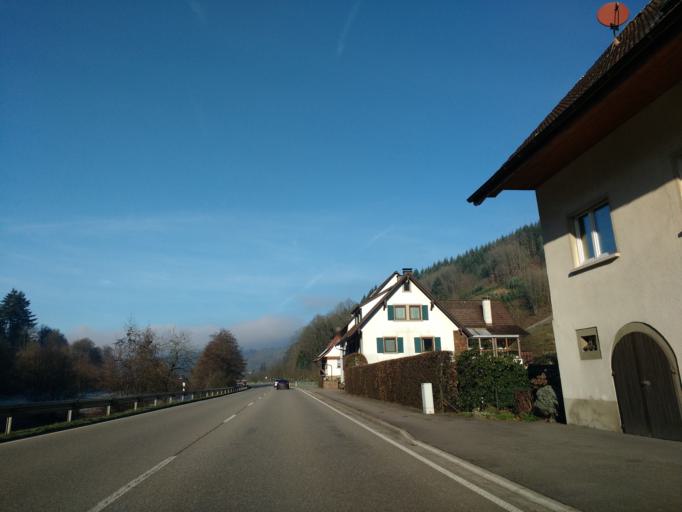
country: DE
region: Baden-Wuerttemberg
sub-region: Freiburg Region
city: Lautenbach
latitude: 48.5122
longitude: 8.1287
